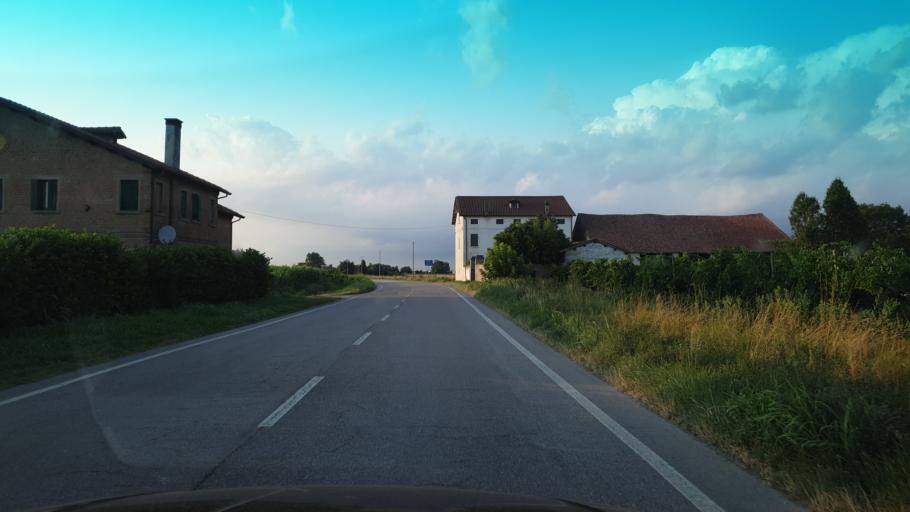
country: IT
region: Veneto
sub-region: Provincia di Rovigo
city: San Bellino
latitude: 45.0582
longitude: 11.5823
